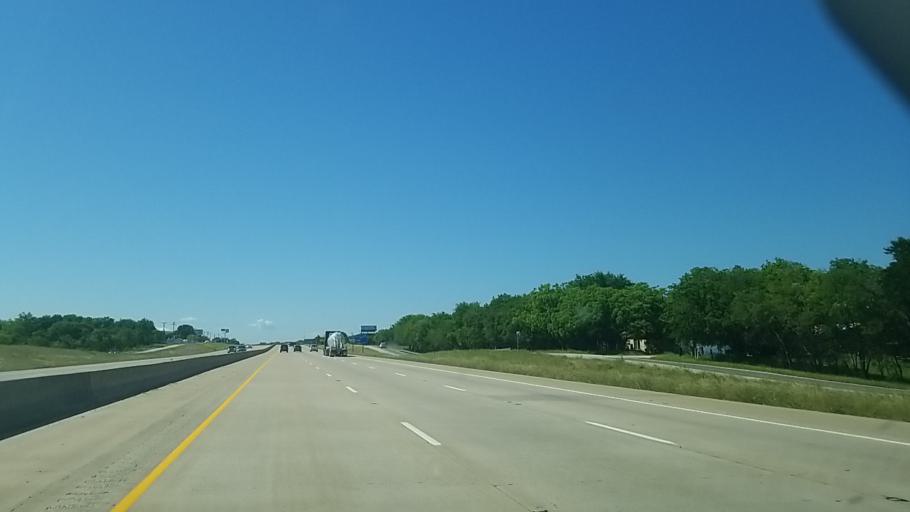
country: US
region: Texas
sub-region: Navarro County
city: Corsicana
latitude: 32.2356
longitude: -96.4919
